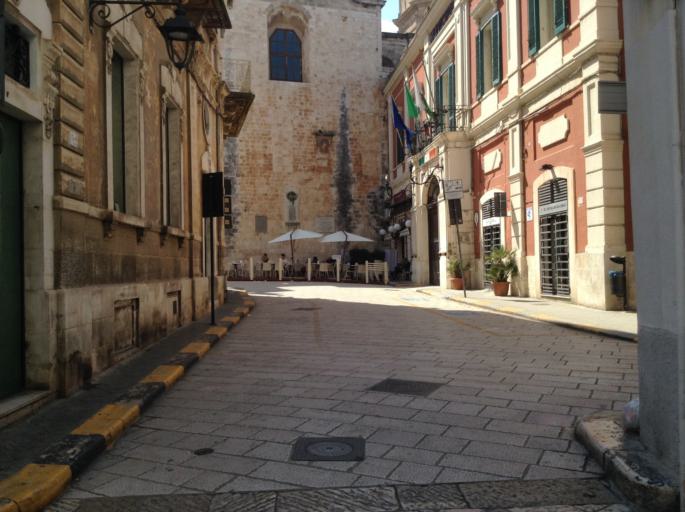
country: IT
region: Apulia
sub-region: Provincia di Bari
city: Monopoli
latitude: 40.9529
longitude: 17.3019
